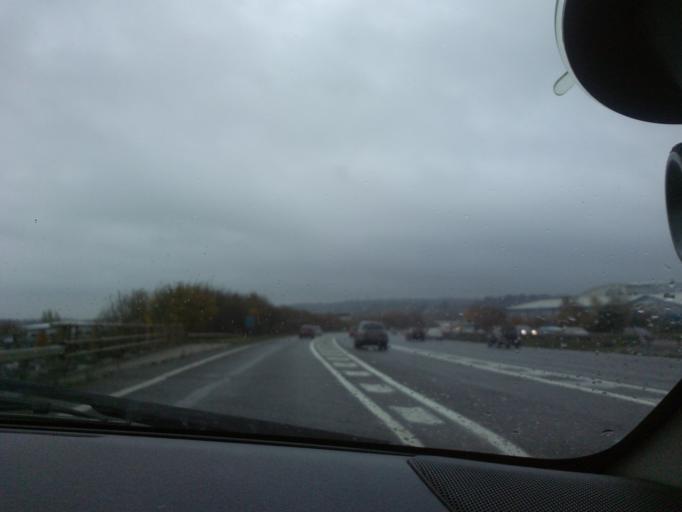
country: GB
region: England
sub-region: Hampshire
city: Eastleigh
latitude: 50.9477
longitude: -1.3663
